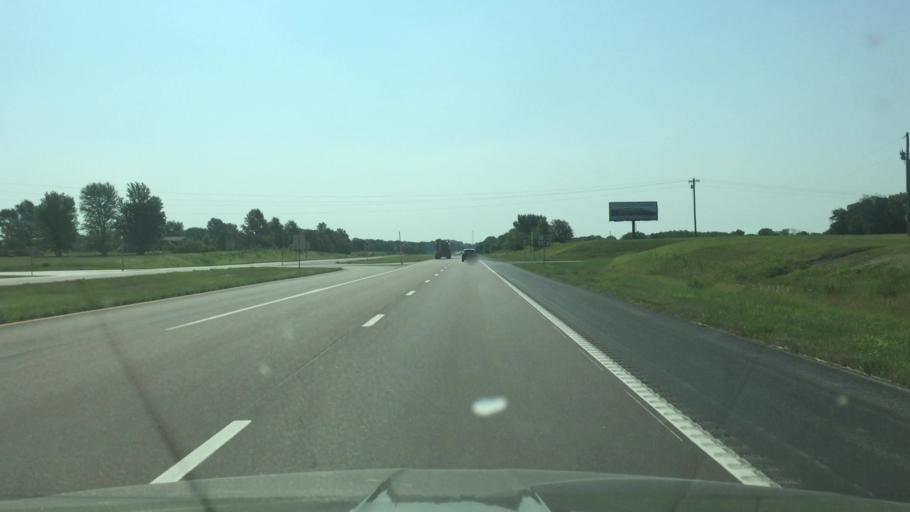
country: US
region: Missouri
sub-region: Pettis County
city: La Monte
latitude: 38.7480
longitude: -93.3422
